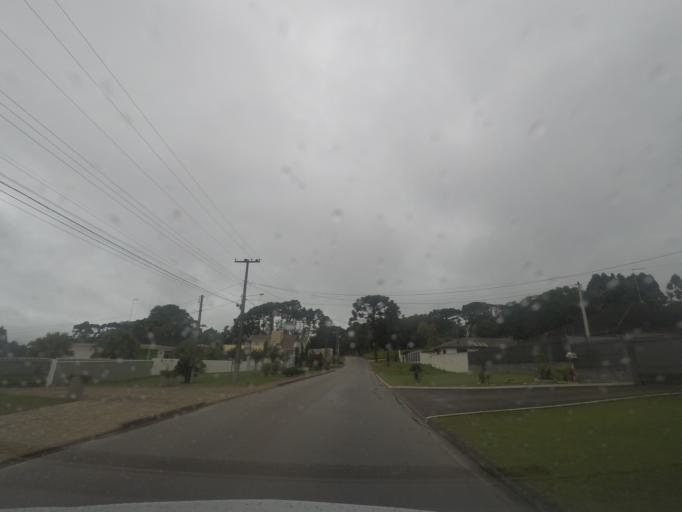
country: BR
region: Parana
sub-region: Campina Grande Do Sul
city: Campina Grande do Sul
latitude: -25.3039
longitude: -49.1250
